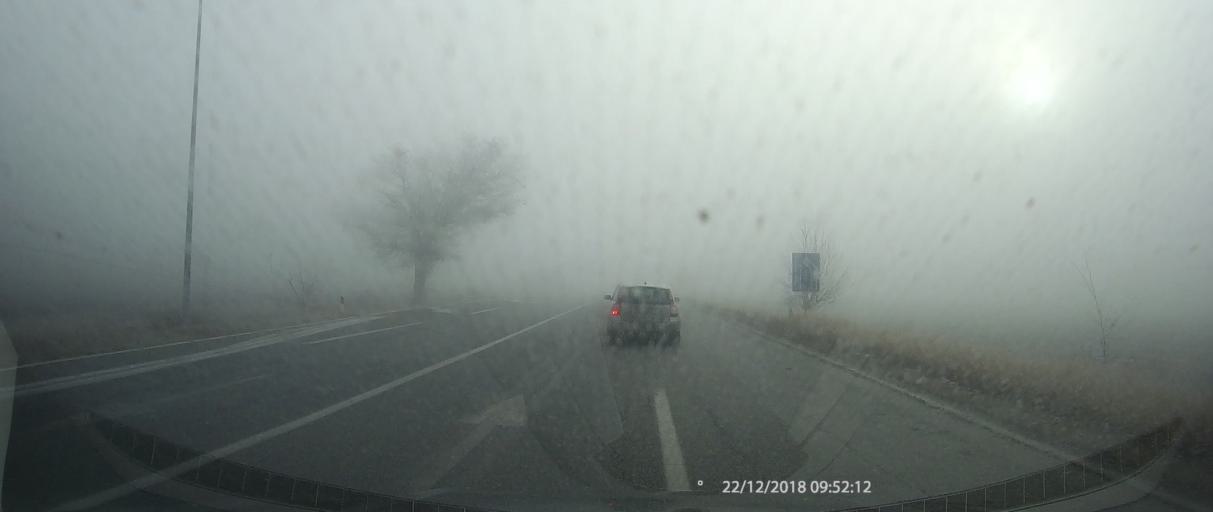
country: MK
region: Staro Nagoricane
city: Staro Nagorichane
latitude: 42.1700
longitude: 21.8190
